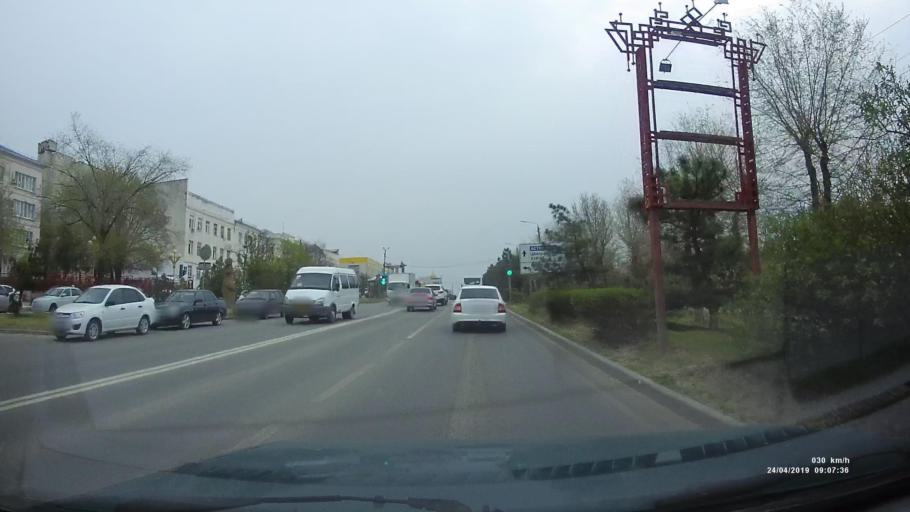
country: RU
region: Kalmykiya
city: Elista
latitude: 46.3073
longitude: 44.2616
